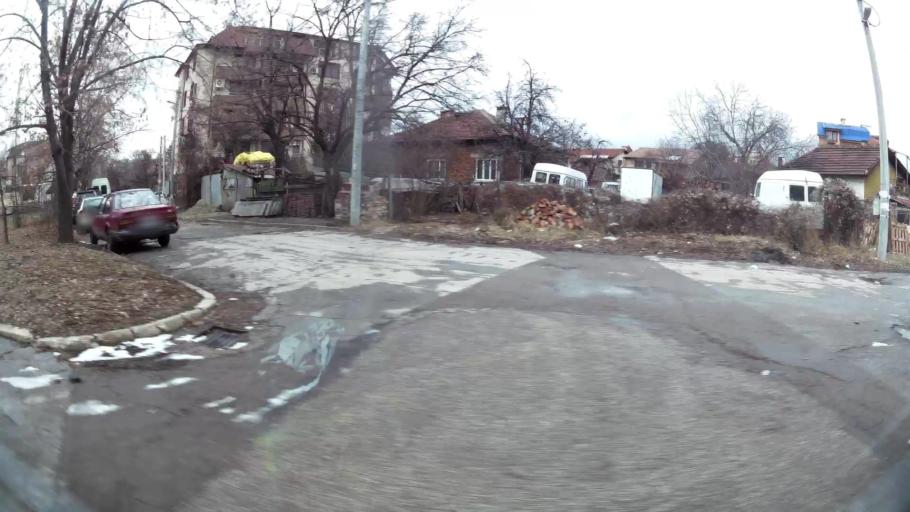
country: BG
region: Sofia-Capital
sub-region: Stolichna Obshtina
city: Sofia
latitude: 42.7208
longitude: 23.3029
